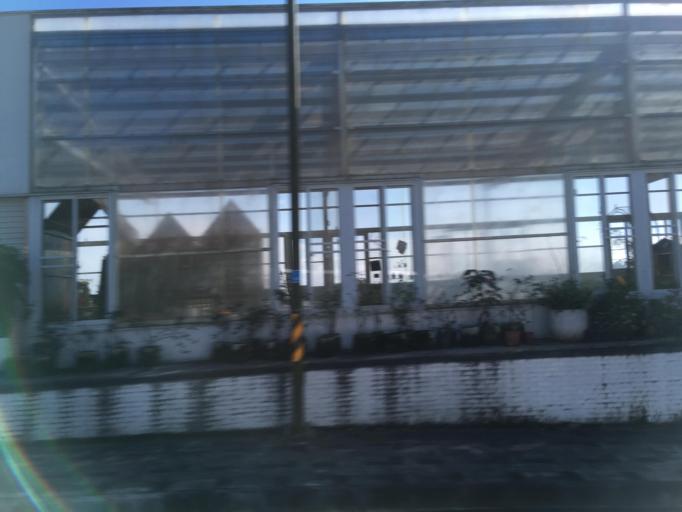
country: TW
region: Taiwan
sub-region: Chiayi
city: Jiayi Shi
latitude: 23.4315
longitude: 120.6636
